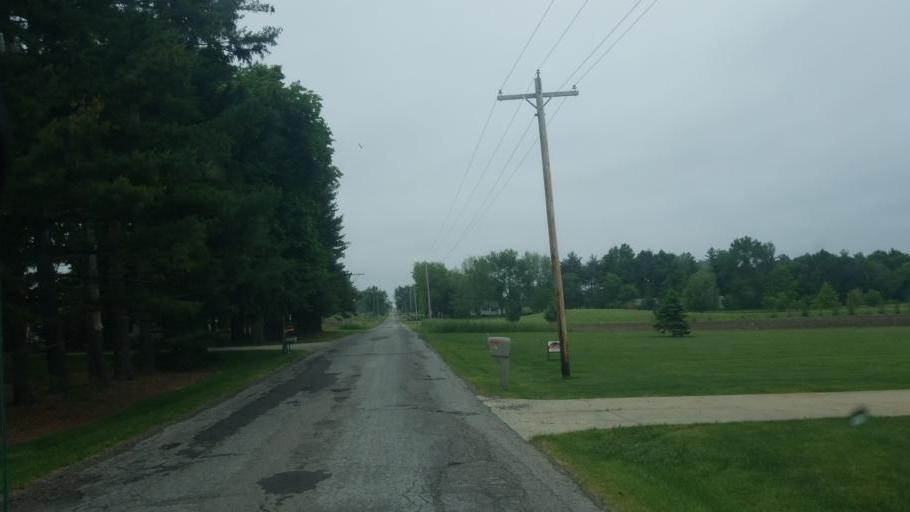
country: US
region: Indiana
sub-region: Marshall County
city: Bremen
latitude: 41.4601
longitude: -86.1176
